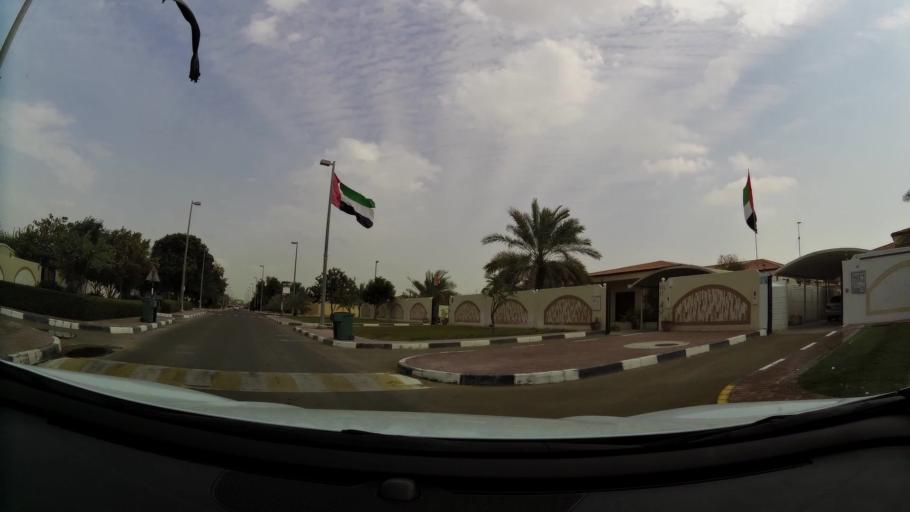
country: AE
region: Abu Dhabi
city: Abu Dhabi
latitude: 24.5196
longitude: 54.6849
